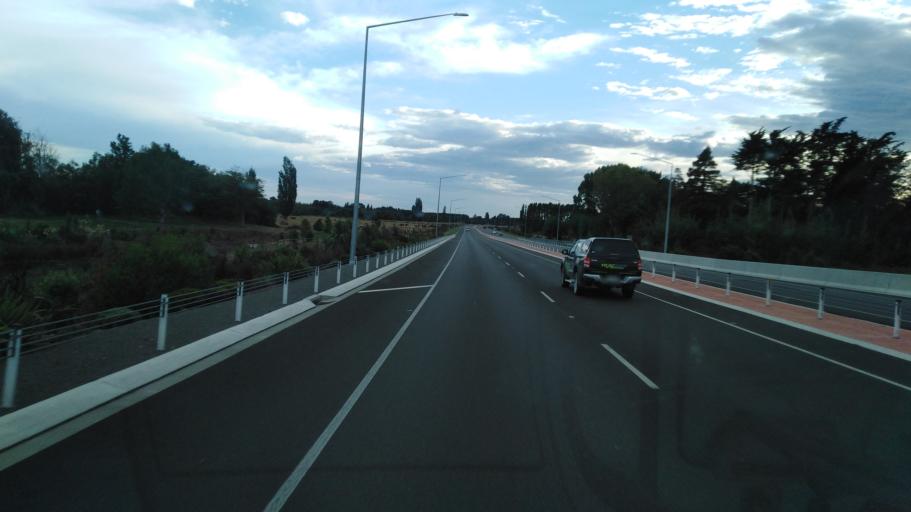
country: NZ
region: Canterbury
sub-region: Waimakariri District
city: Kaiapoi
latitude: -43.4480
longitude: 172.6127
